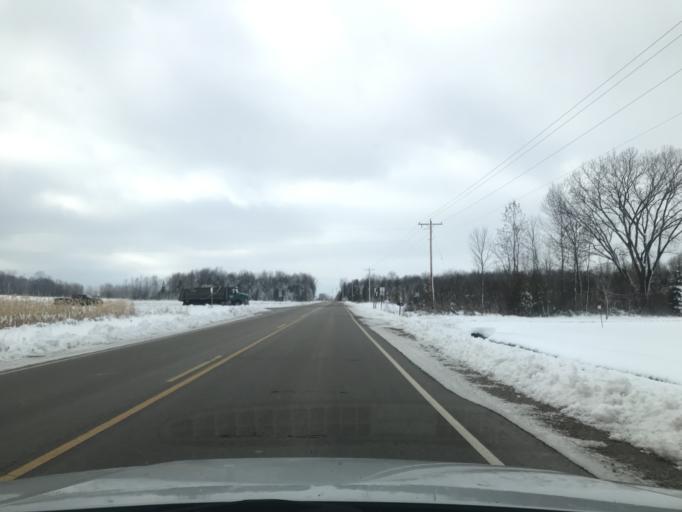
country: US
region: Wisconsin
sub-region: Oconto County
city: Oconto
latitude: 44.9505
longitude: -87.9863
